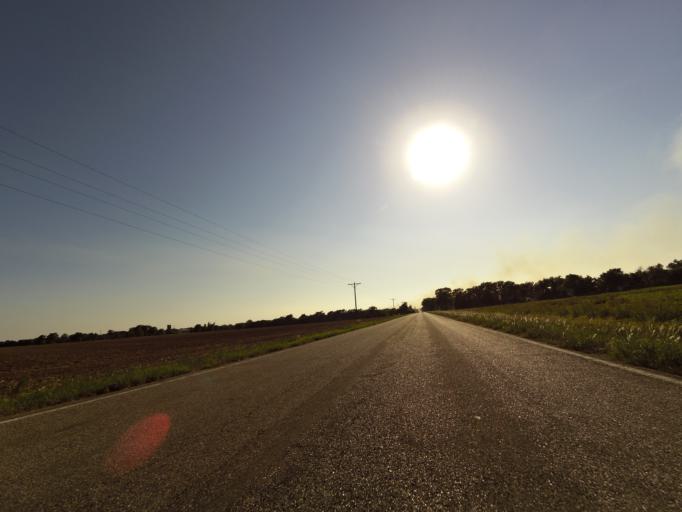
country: US
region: Kansas
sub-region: McPherson County
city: Moundridge
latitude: 38.1451
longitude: -97.5301
